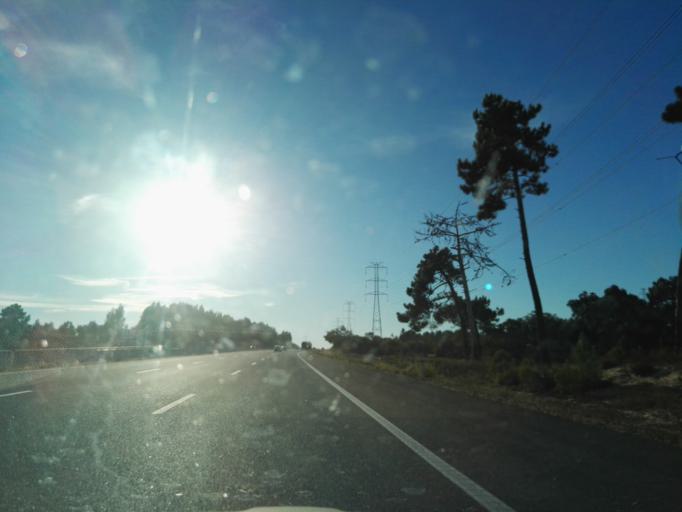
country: PT
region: Setubal
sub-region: Palmela
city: Quinta do Anjo
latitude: 38.5840
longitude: -8.9520
